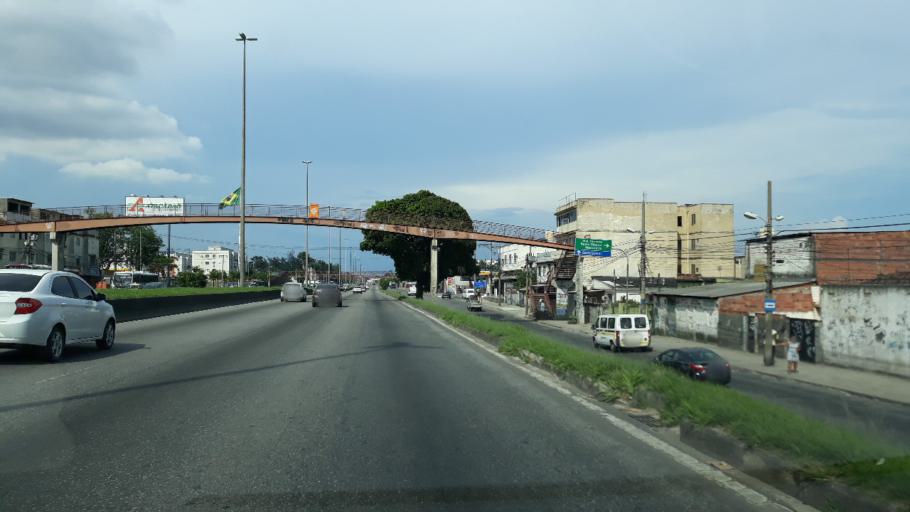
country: BR
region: Rio de Janeiro
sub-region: Sao Joao De Meriti
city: Sao Joao de Meriti
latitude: -22.8447
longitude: -43.3765
